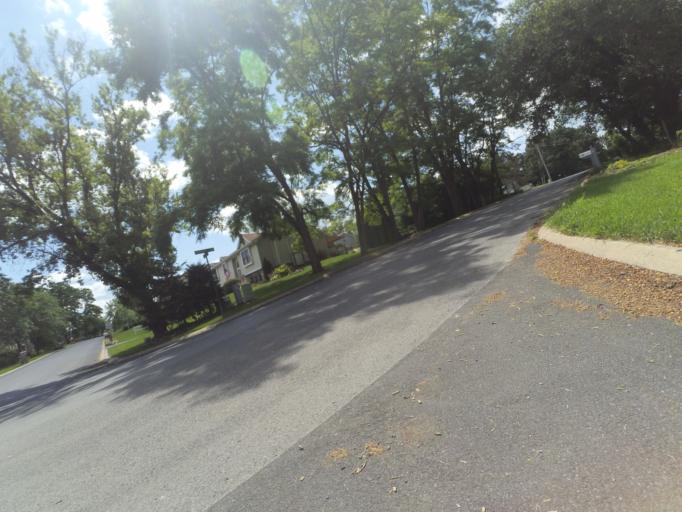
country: US
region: Pennsylvania
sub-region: Centre County
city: Lemont
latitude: 40.8058
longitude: -77.8296
